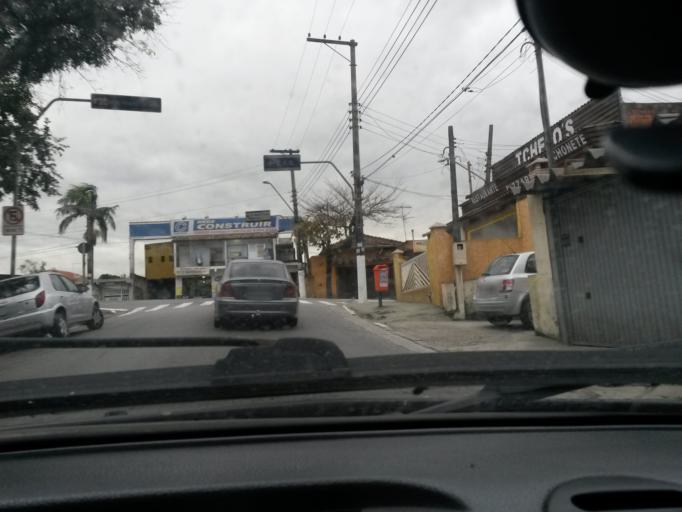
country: BR
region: Sao Paulo
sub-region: Sao Bernardo Do Campo
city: Sao Bernardo do Campo
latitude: -23.7800
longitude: -46.5320
